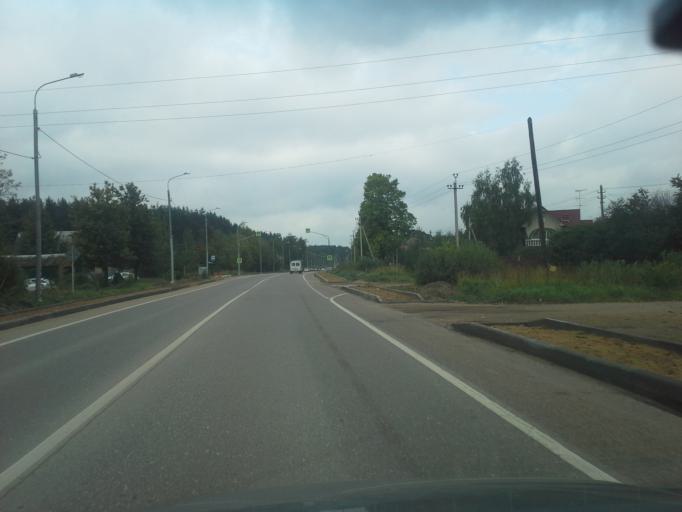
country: RU
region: Moskovskaya
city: Kubinka
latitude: 55.5722
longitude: 36.6878
